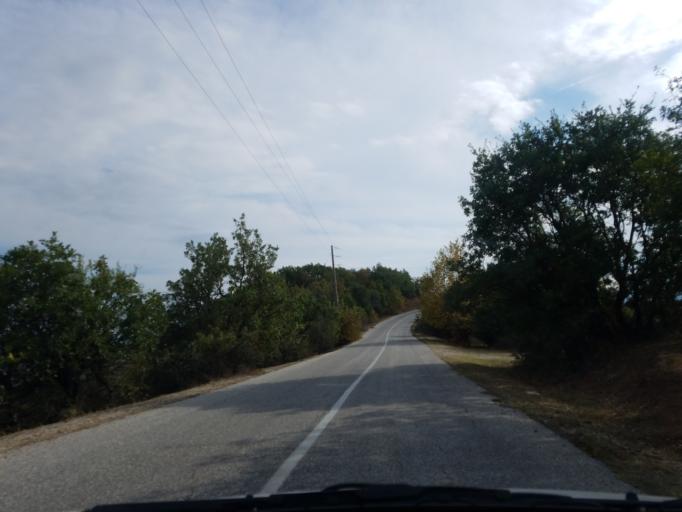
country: GR
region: Thessaly
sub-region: Trikala
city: Kastraki
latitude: 39.7380
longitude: 21.6554
